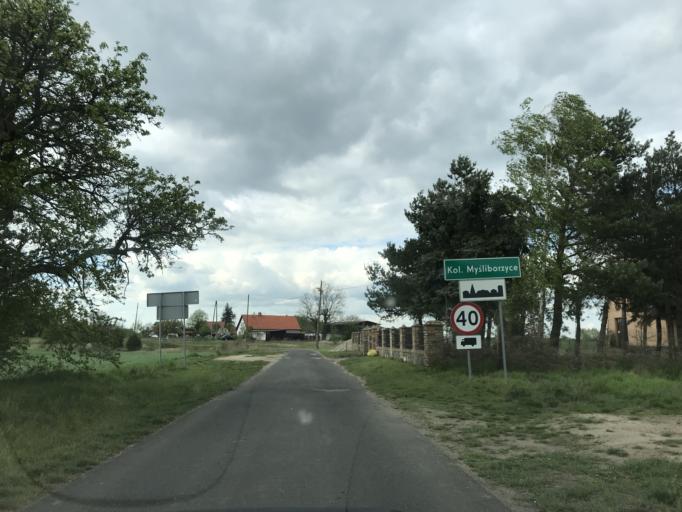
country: PL
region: West Pomeranian Voivodeship
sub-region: Powiat mysliborski
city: Mysliborz
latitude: 52.8844
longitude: 14.8984
